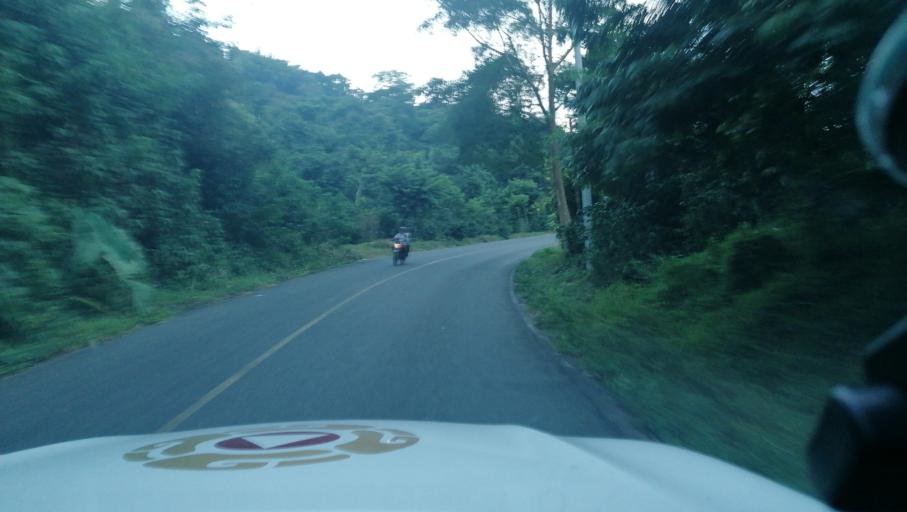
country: MX
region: Chiapas
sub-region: Cacahoatan
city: Benito Juarez
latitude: 15.0473
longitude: -92.2433
